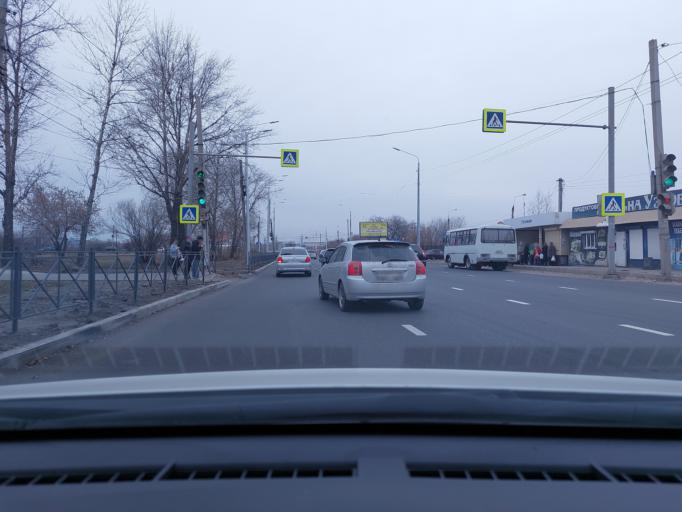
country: RU
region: Irkutsk
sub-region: Irkutskiy Rayon
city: Irkutsk
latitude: 52.3292
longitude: 104.2342
